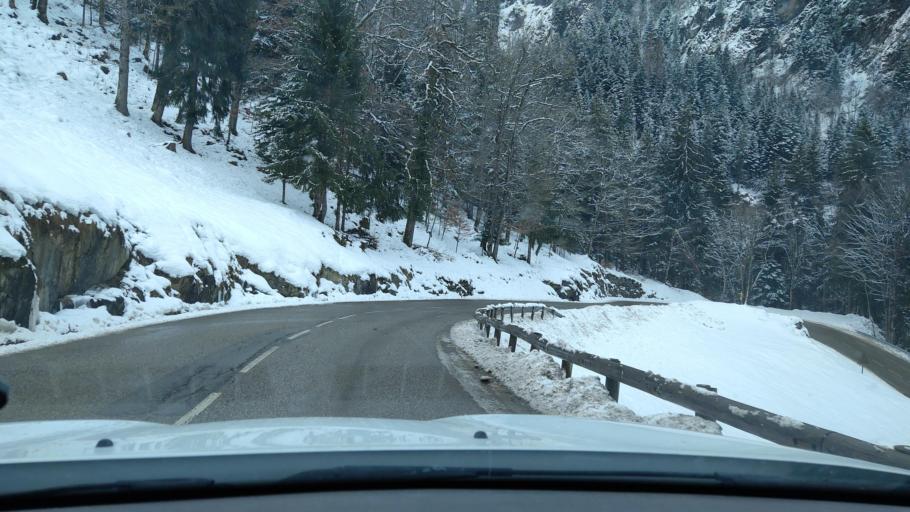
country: FR
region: Rhone-Alpes
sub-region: Departement de la Savoie
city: Beaufort
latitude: 45.7159
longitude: 6.5790
